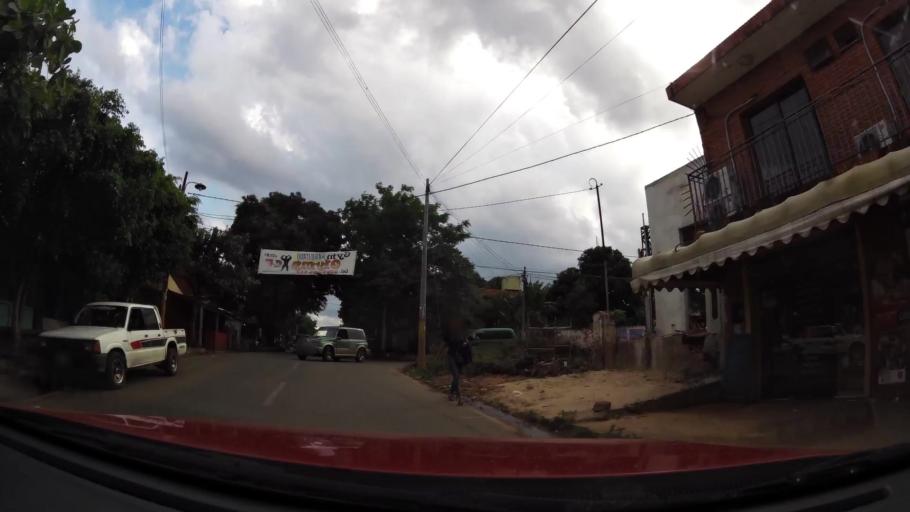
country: PY
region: Central
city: Villa Elisa
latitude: -25.3476
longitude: -57.5640
